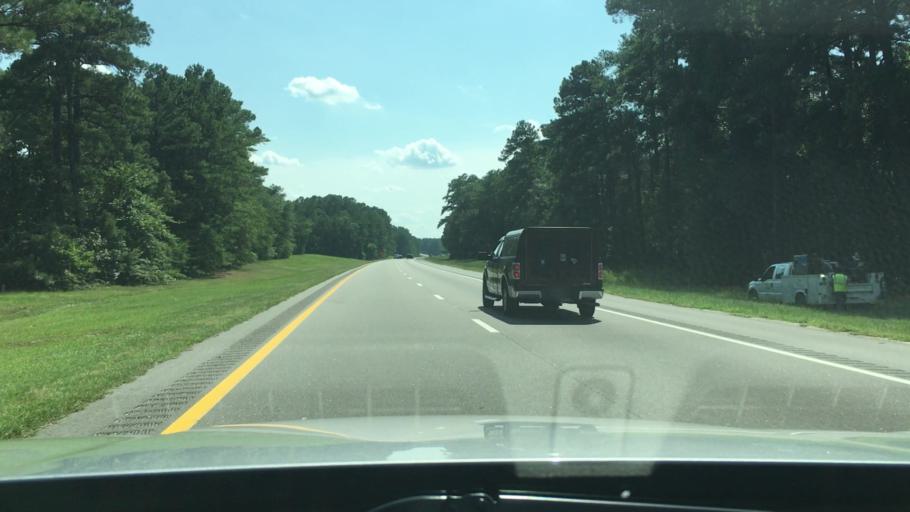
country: US
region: North Carolina
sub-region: Cumberland County
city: Hope Mills
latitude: 34.9455
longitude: -78.9093
